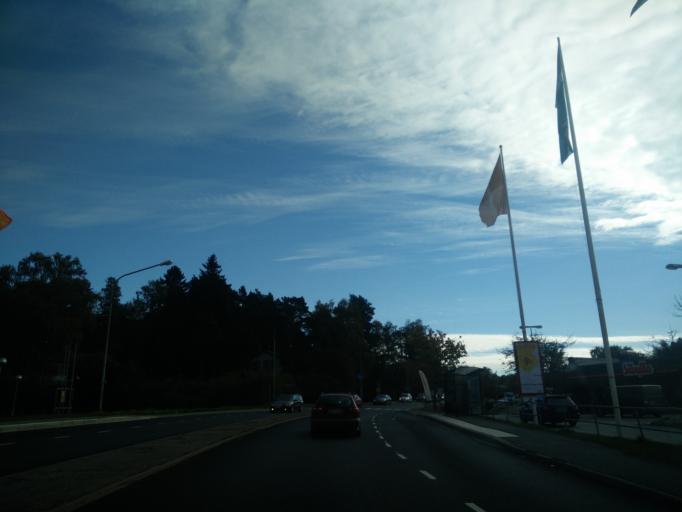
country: SE
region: Stockholm
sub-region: Upplands Vasby Kommun
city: Upplands Vaesby
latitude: 59.5141
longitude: 17.9292
